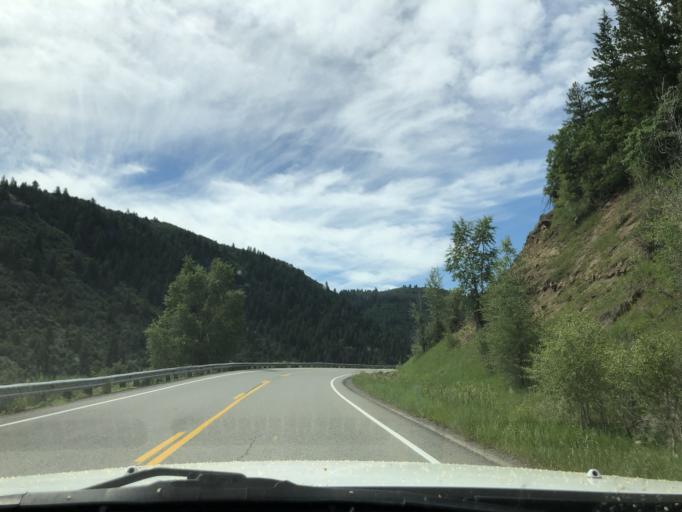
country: US
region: Colorado
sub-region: Delta County
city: Paonia
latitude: 38.9659
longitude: -107.3389
